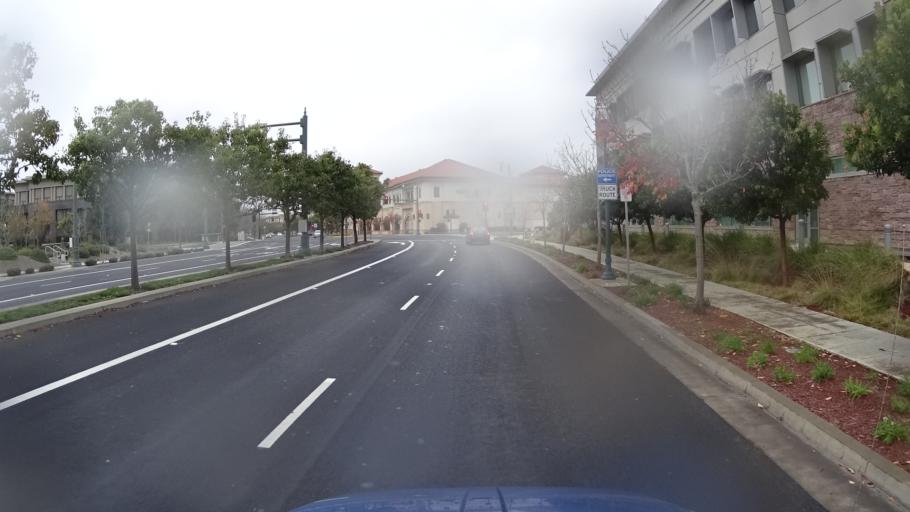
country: US
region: California
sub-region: San Mateo County
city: Foster City
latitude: 37.5427
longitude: -122.2914
